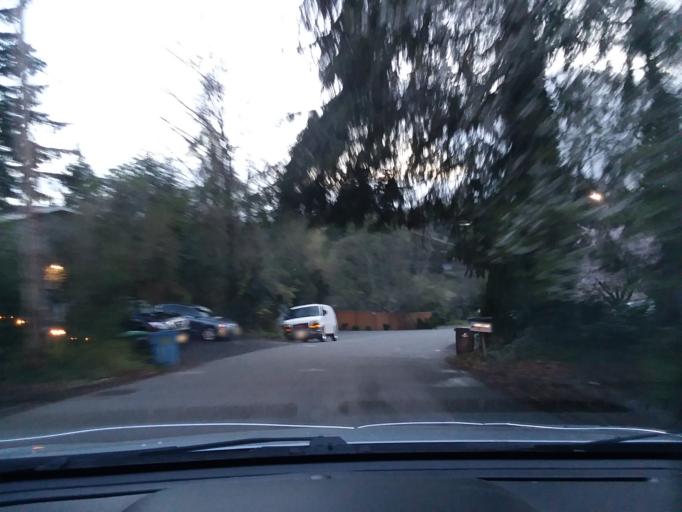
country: US
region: Washington
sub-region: Snohomish County
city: Mountlake Terrace
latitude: 47.7651
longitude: -122.3173
